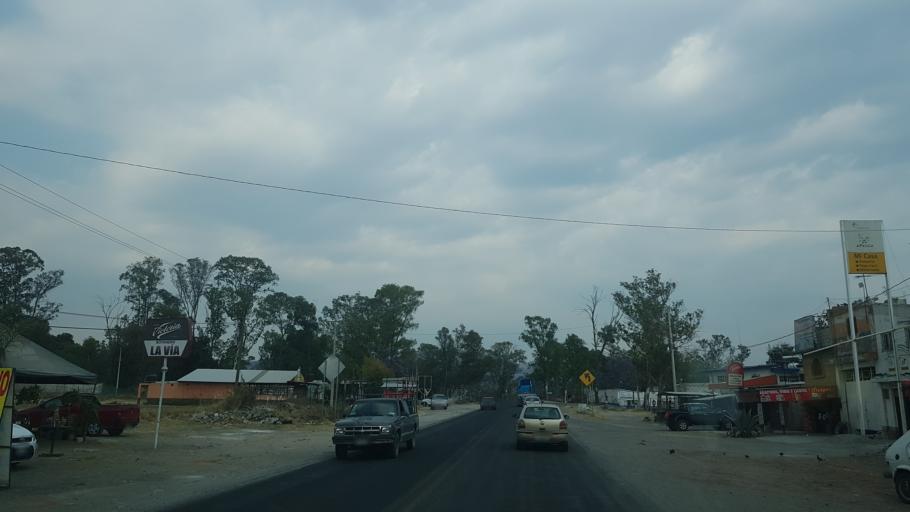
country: MX
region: Puebla
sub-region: Santa Isabel Cholula
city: Santa Ana Acozautla
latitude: 18.9441
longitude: -98.3931
